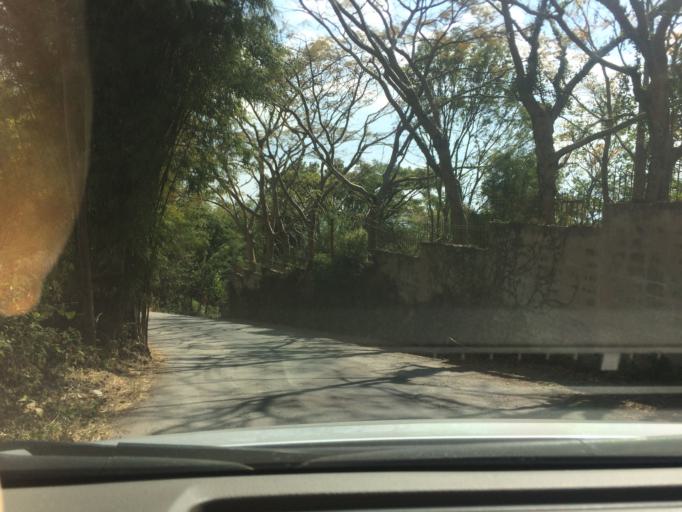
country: TH
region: Phetchabun
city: Khao Kho
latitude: 16.7831
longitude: 101.0408
